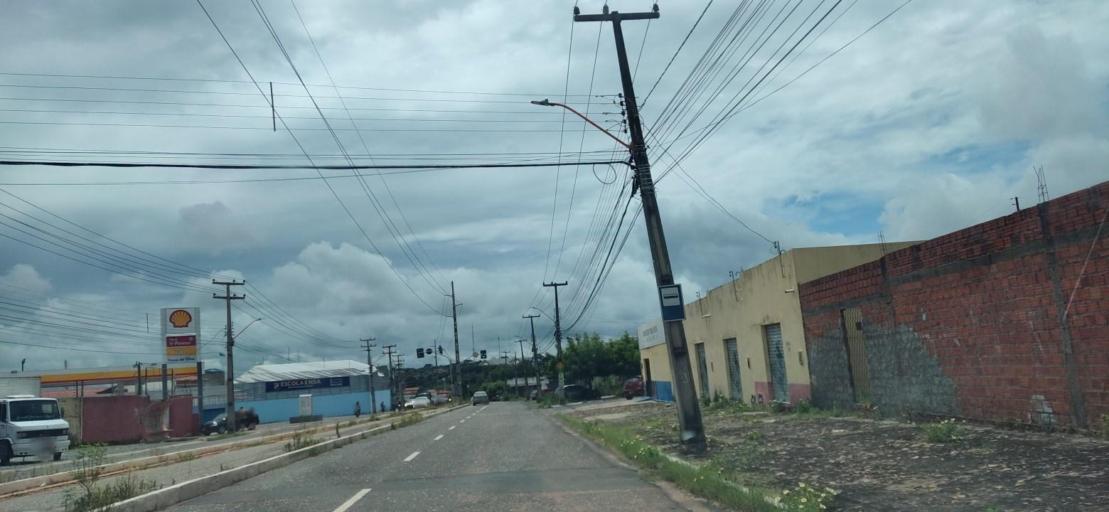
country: BR
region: Piaui
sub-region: Teresina
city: Teresina
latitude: -5.0625
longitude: -42.7577
